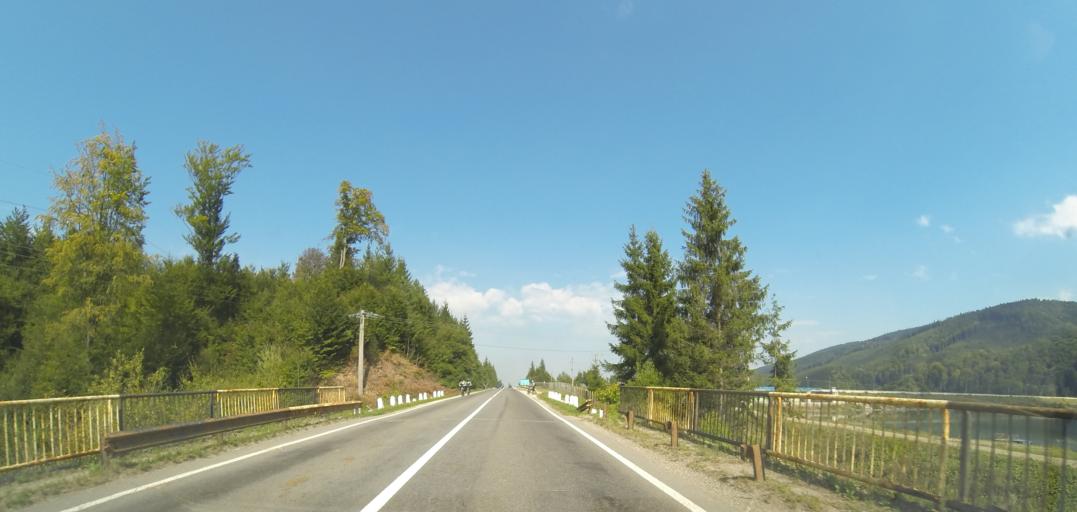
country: RO
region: Brasov
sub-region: Comuna Tarlungeni
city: Tarlungeni
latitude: 45.5789
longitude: 25.7612
